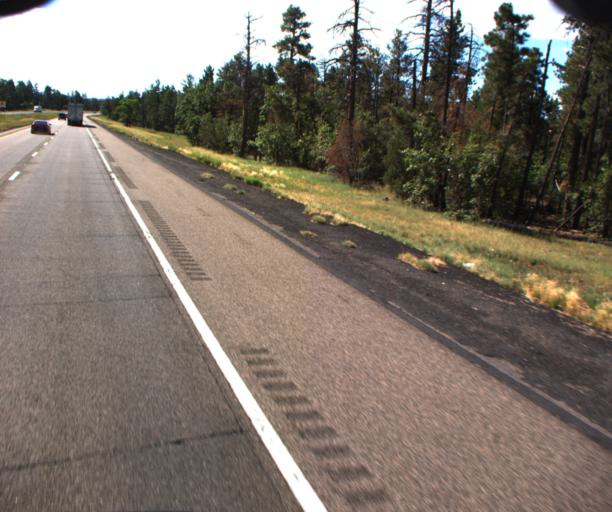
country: US
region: Arizona
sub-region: Coconino County
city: Sedona
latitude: 34.8600
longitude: -111.6145
